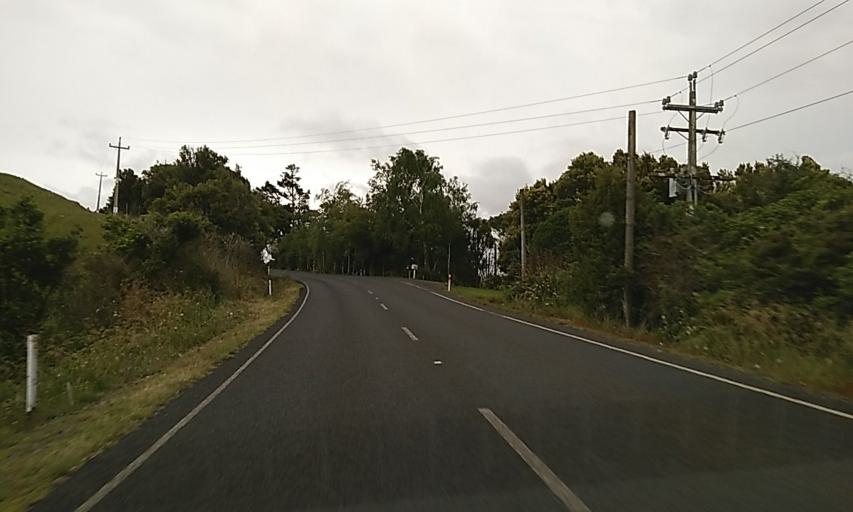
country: NZ
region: Auckland
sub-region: Auckland
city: Pukekohe East
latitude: -37.3192
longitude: 174.9307
